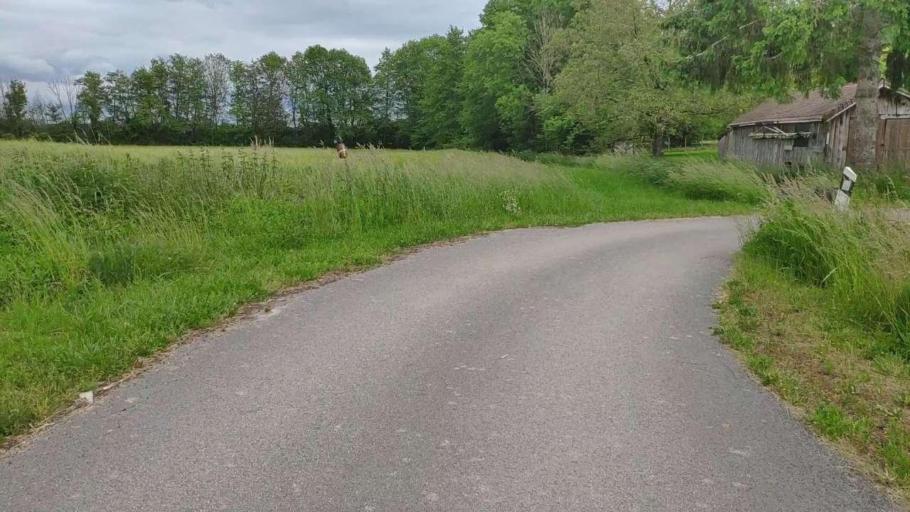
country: FR
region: Franche-Comte
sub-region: Departement du Jura
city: Montmorot
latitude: 46.7613
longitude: 5.5452
